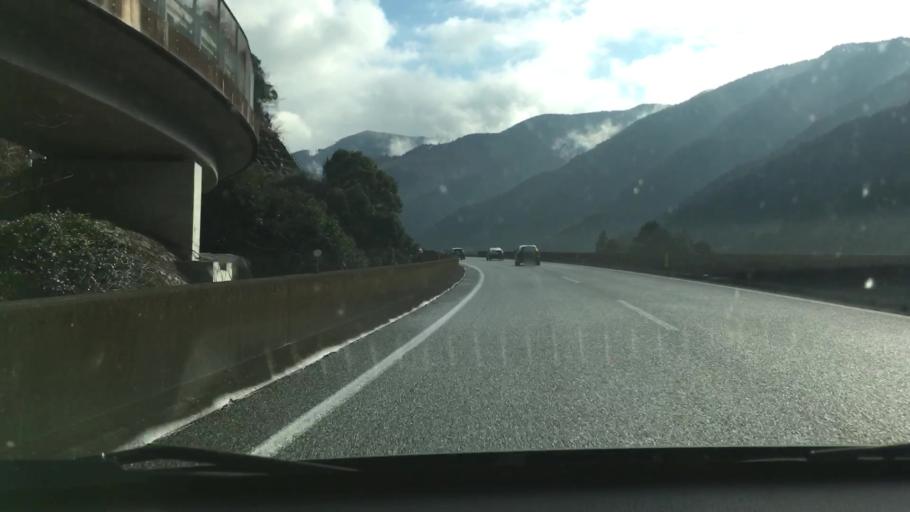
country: JP
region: Kumamoto
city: Yatsushiro
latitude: 32.4130
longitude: 130.6955
